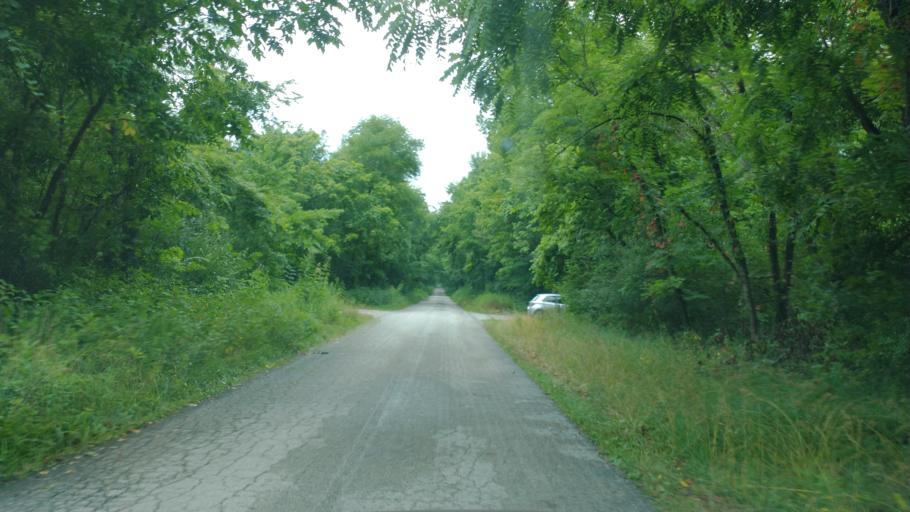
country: US
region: Ohio
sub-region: Meigs County
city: Middleport
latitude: 38.9322
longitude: -82.0731
